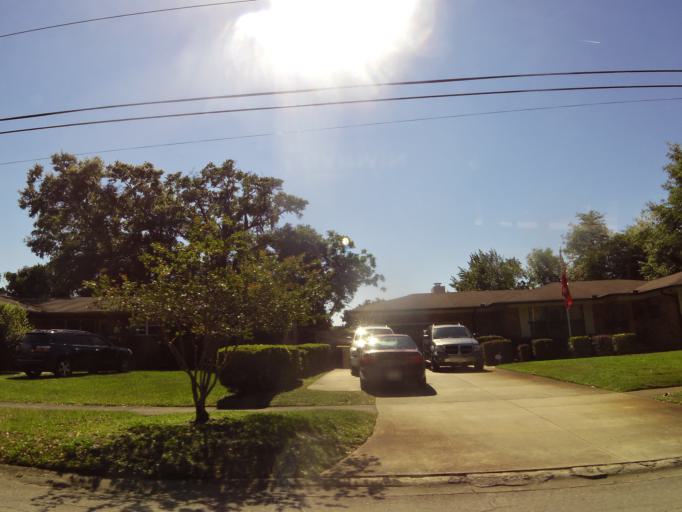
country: US
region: Florida
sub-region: Duval County
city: Jacksonville
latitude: 30.3393
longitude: -81.5685
